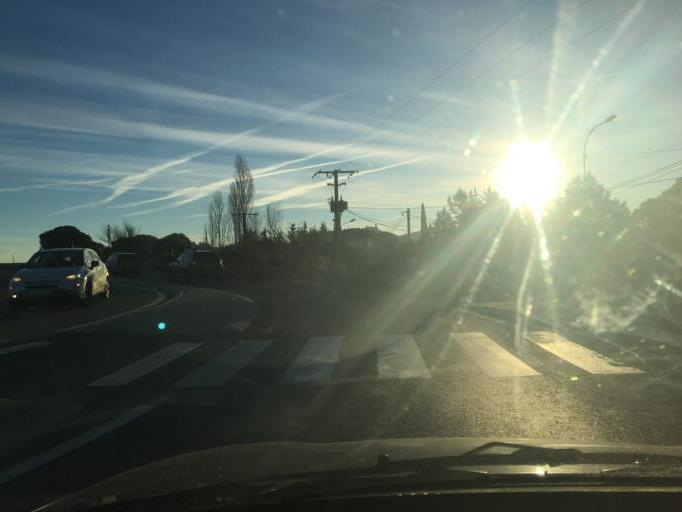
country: FR
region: Provence-Alpes-Cote d'Azur
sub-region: Departement du Var
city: Le Muy
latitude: 43.4661
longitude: 6.5439
